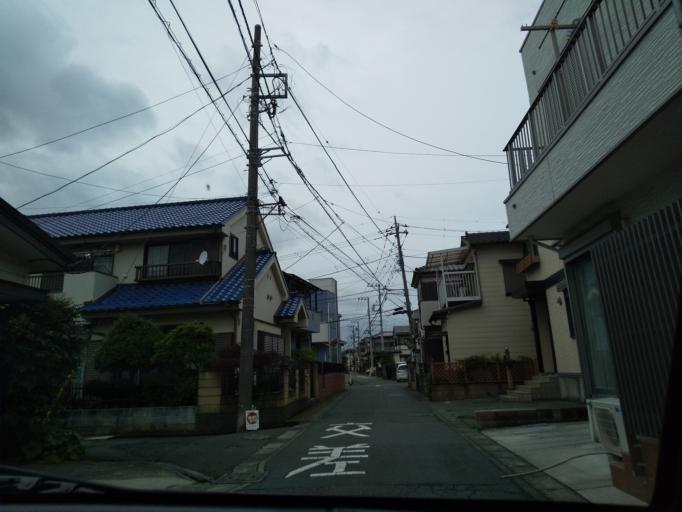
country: JP
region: Kanagawa
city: Minami-rinkan
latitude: 35.4325
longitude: 139.4436
